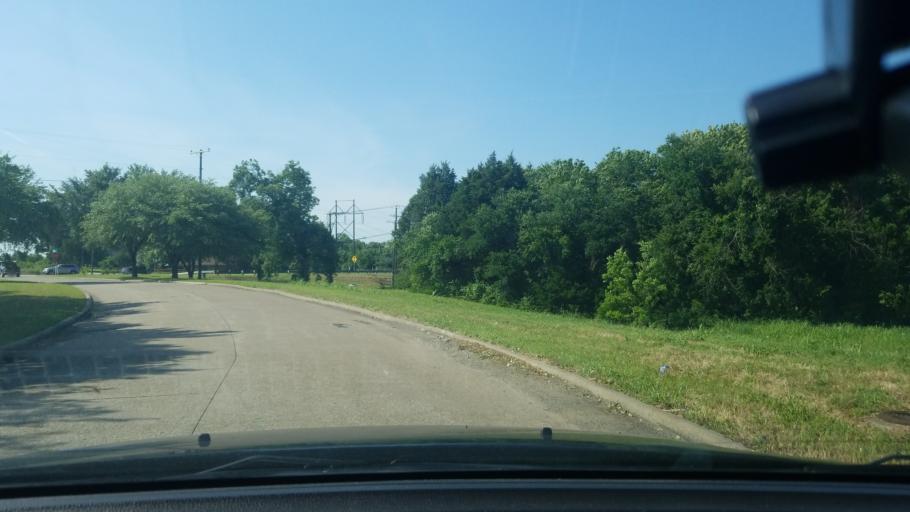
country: US
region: Texas
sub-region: Dallas County
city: Mesquite
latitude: 32.7729
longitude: -96.5740
